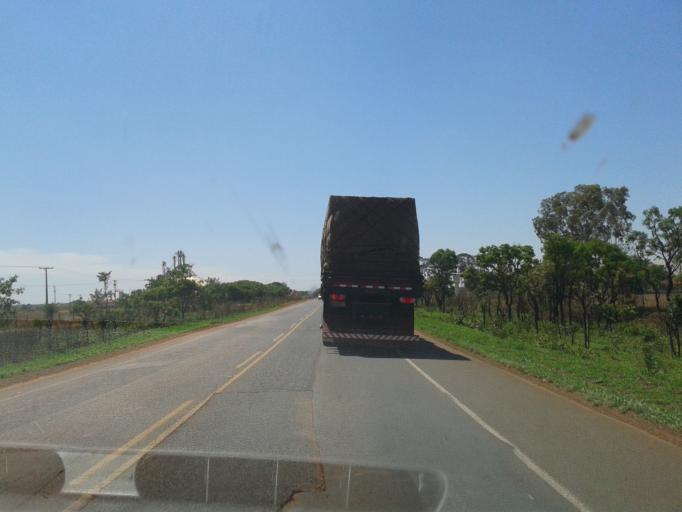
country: BR
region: Minas Gerais
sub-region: Sacramento
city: Sacramento
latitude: -19.2976
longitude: -47.4942
